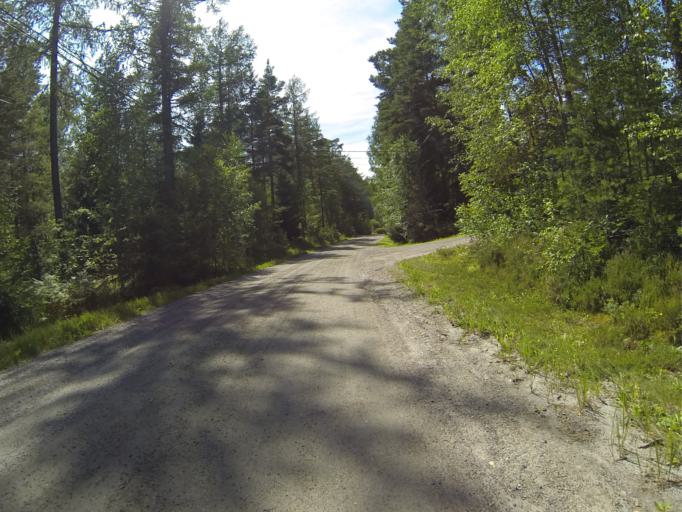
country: FI
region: Varsinais-Suomi
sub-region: Salo
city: Saerkisalo
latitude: 60.2613
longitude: 22.9739
